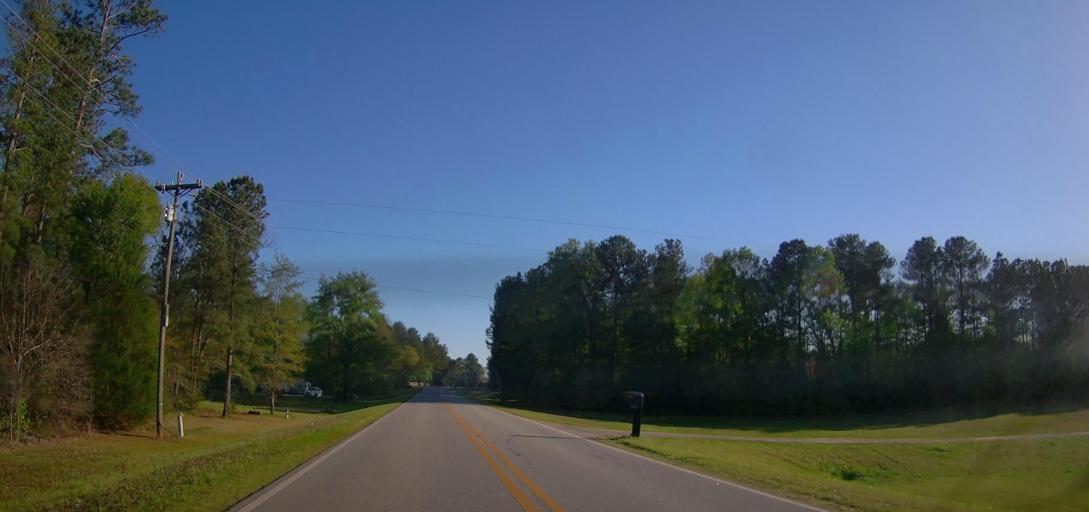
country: US
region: Georgia
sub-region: Butts County
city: Indian Springs
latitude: 33.2803
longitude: -83.8967
